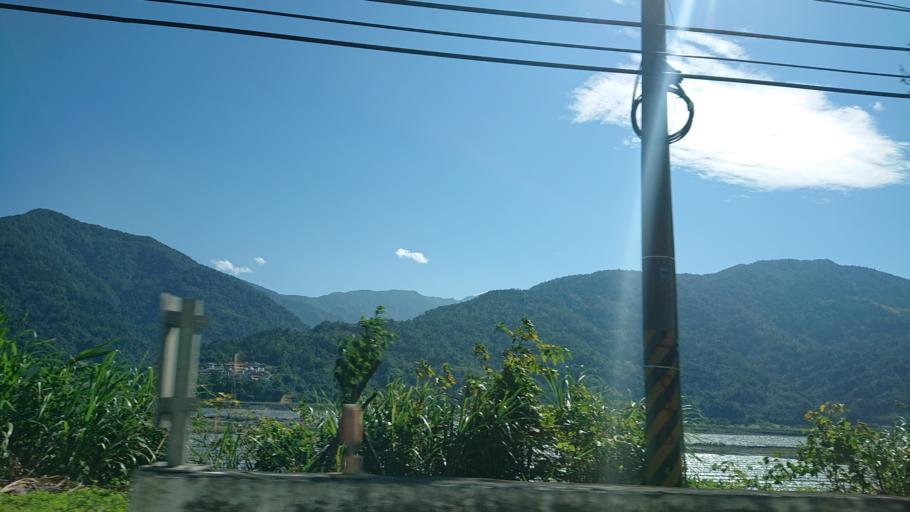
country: TW
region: Taiwan
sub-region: Yilan
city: Yilan
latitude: 24.6052
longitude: 121.5214
